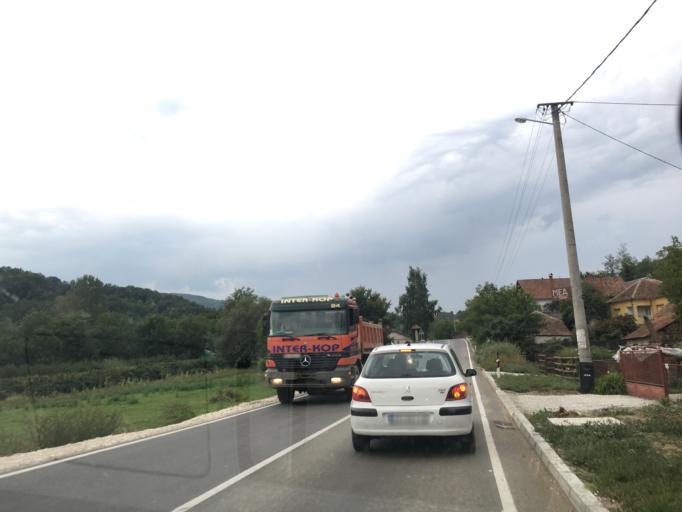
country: RS
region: Central Serbia
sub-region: Sumadijski Okrug
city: Arangelovac
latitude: 44.1892
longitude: 20.5681
